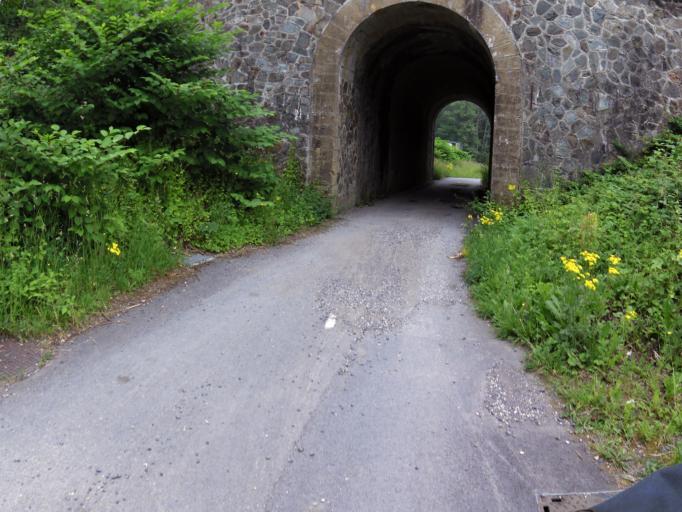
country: FR
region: Champagne-Ardenne
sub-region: Departement des Ardennes
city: Fumay
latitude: 49.9789
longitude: 4.6870
